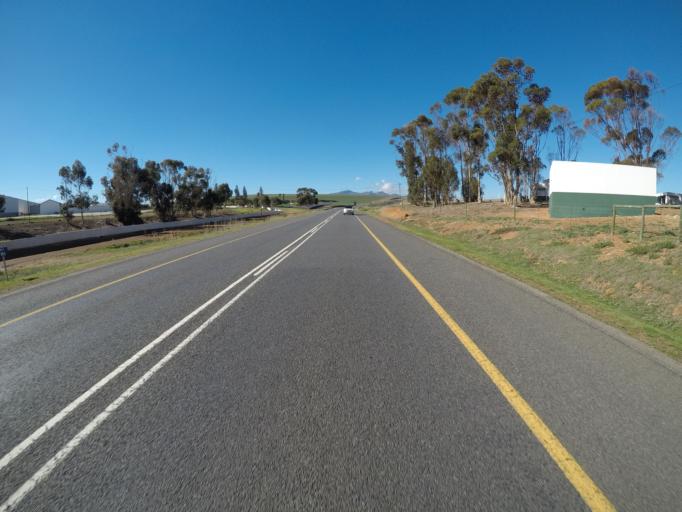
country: ZA
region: Western Cape
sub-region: Overberg District Municipality
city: Caledon
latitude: -34.2112
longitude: 19.3384
